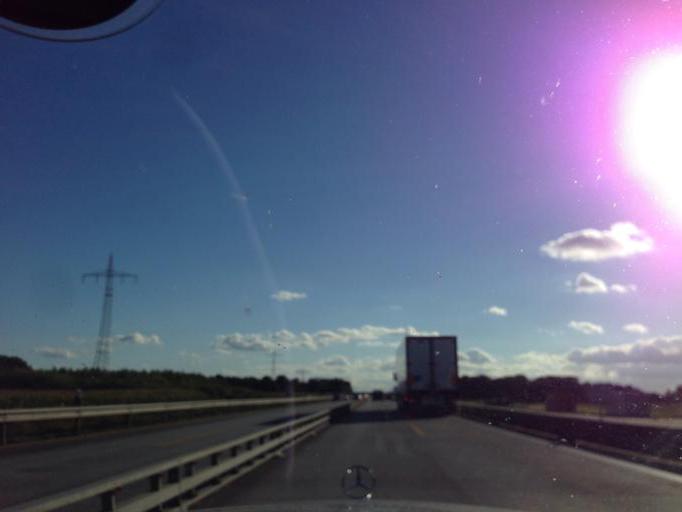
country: DE
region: Schleswig-Holstein
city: Krogaspe
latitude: 54.1024
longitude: 9.9382
